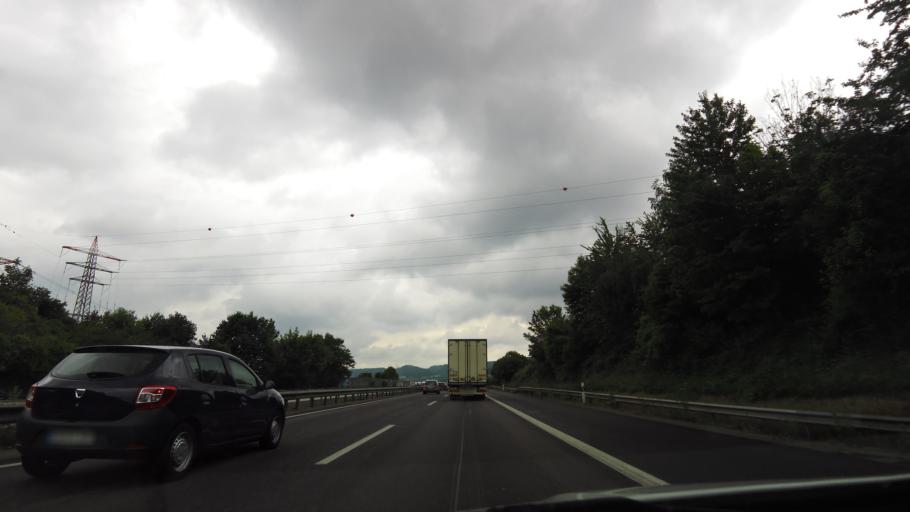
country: DE
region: Rheinland-Pfalz
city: Bad Neuenahr-Ahrweiler
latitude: 50.5530
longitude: 7.1536
